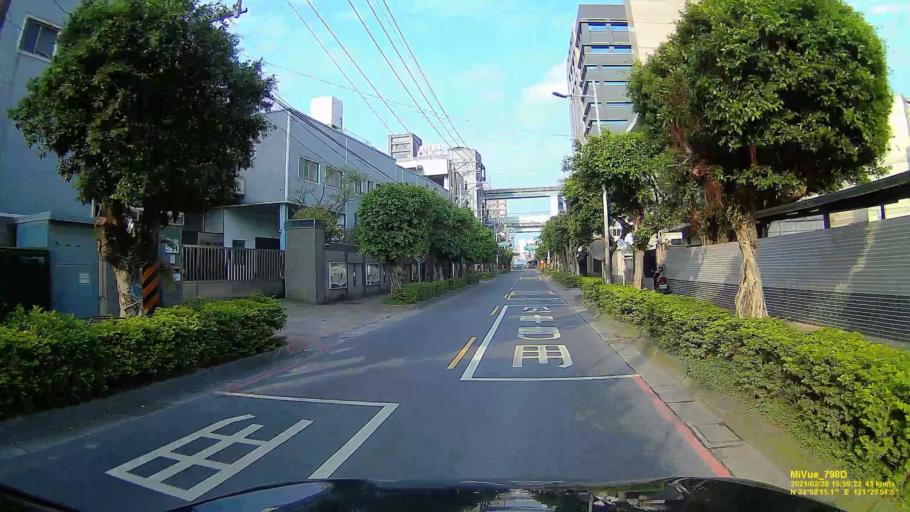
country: TW
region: Taipei
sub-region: Taipei
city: Banqiao
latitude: 24.9699
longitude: 121.4320
